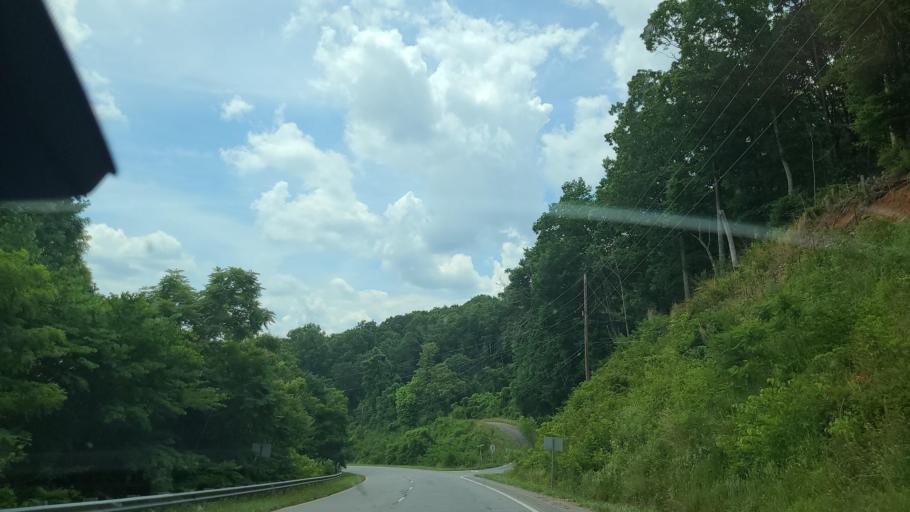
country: US
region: Georgia
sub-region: Fannin County
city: McCaysville
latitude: 35.0173
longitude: -84.2889
